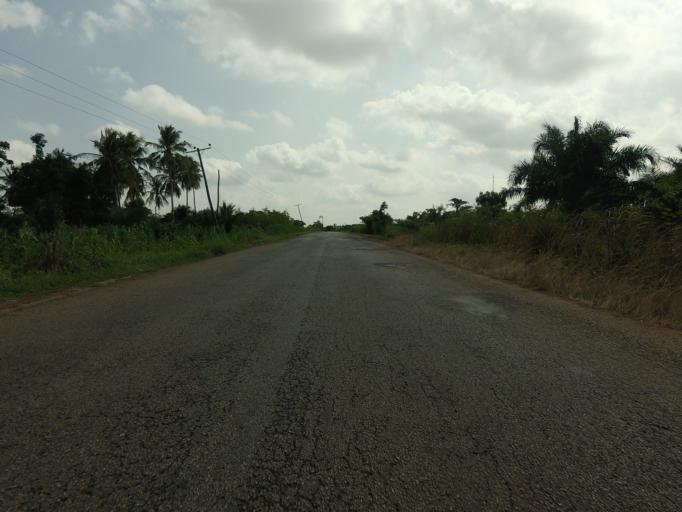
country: GH
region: Volta
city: Ho
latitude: 6.4158
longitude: 0.7508
